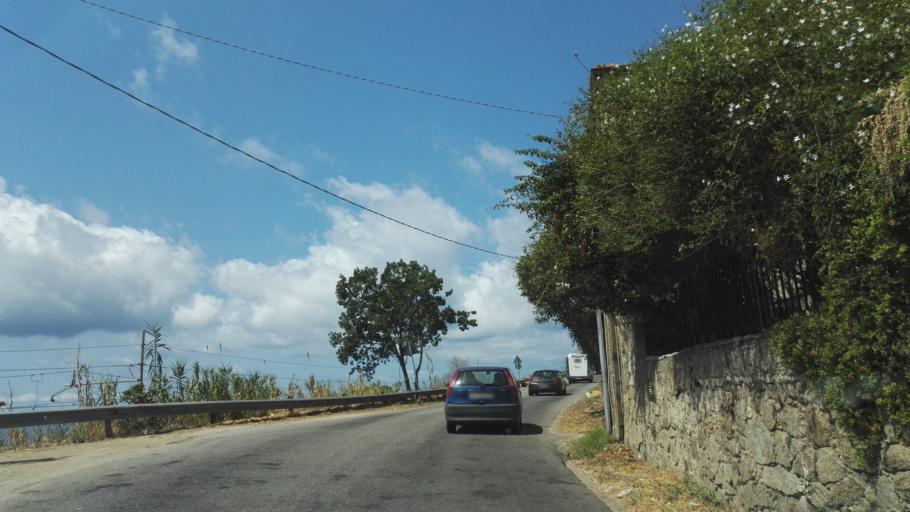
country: IT
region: Calabria
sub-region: Provincia di Vibo-Valentia
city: Nicotera
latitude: 38.5476
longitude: 15.9421
